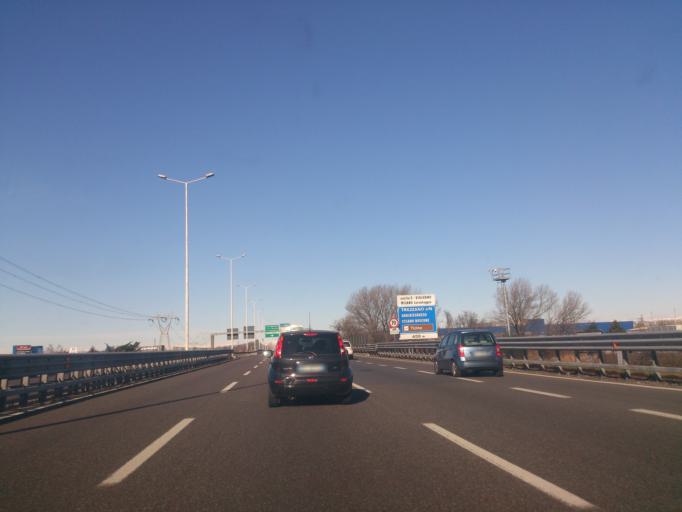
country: IT
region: Lombardy
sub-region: Citta metropolitana di Milano
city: Trezzano sul Naviglio
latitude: 45.4220
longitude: 9.0804
